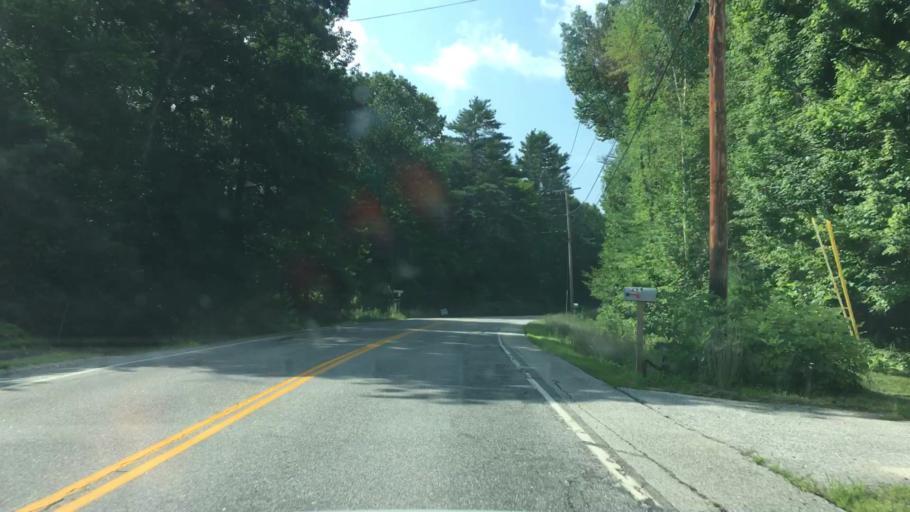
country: US
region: Maine
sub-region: Cumberland County
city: Raymond
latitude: 43.9216
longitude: -70.4353
